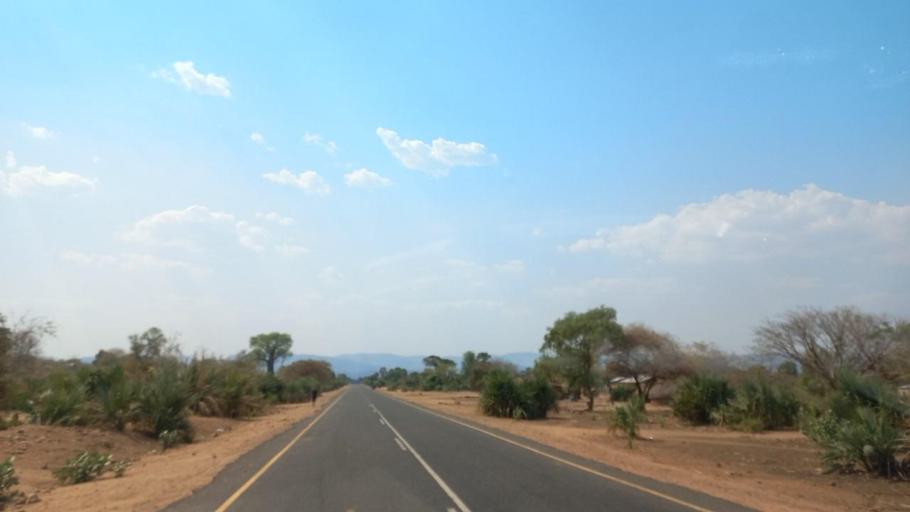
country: ZM
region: Lusaka
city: Luangwa
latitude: -15.1142
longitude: 30.2053
